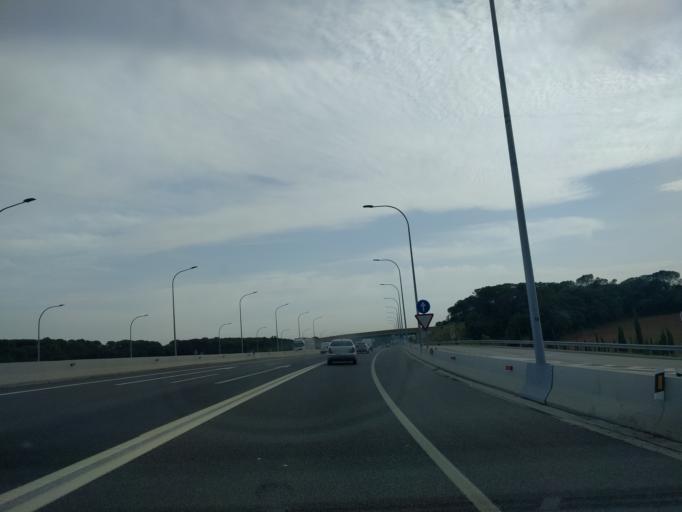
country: ES
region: Catalonia
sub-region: Provincia de Girona
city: Fornells de la Selva
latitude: 41.9246
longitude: 2.7931
